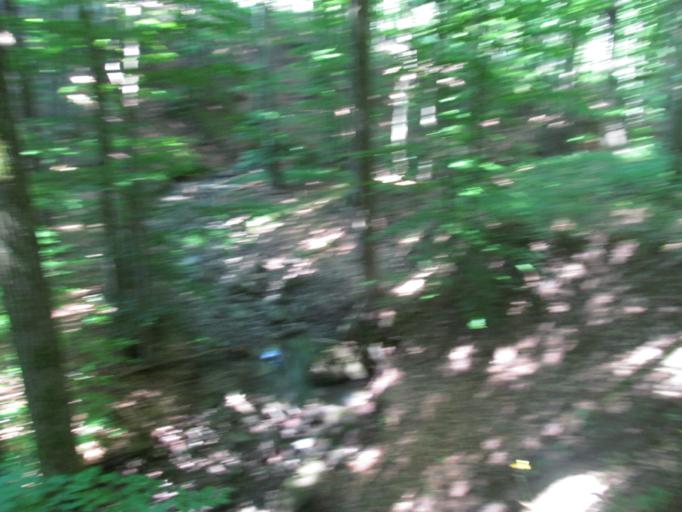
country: HU
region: Pest
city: Pilisszentkereszt
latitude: 47.7255
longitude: 18.9187
